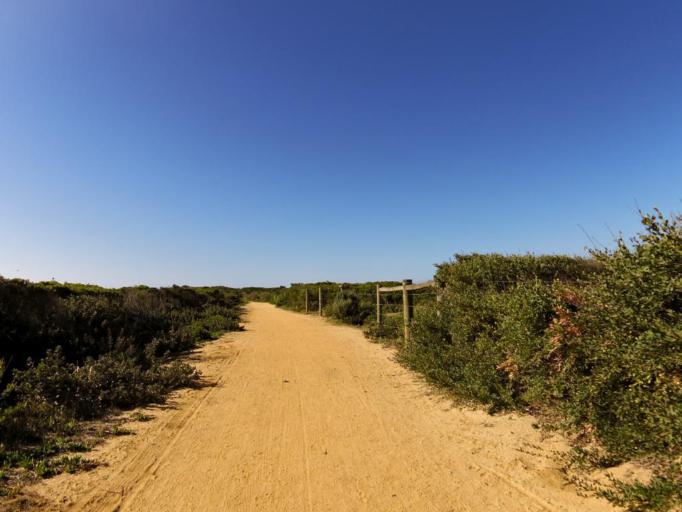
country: AU
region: Victoria
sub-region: Bass Coast
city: North Wonthaggi
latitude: -38.5584
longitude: 145.4878
